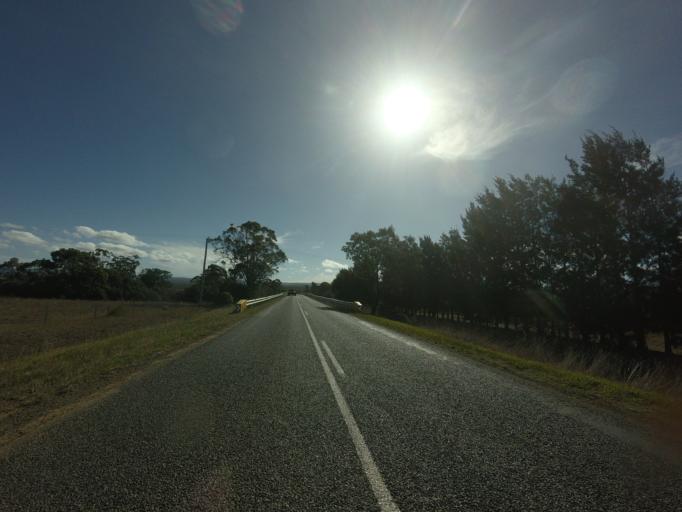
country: AU
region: Tasmania
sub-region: Break O'Day
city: St Helens
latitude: -41.9971
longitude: 148.0817
